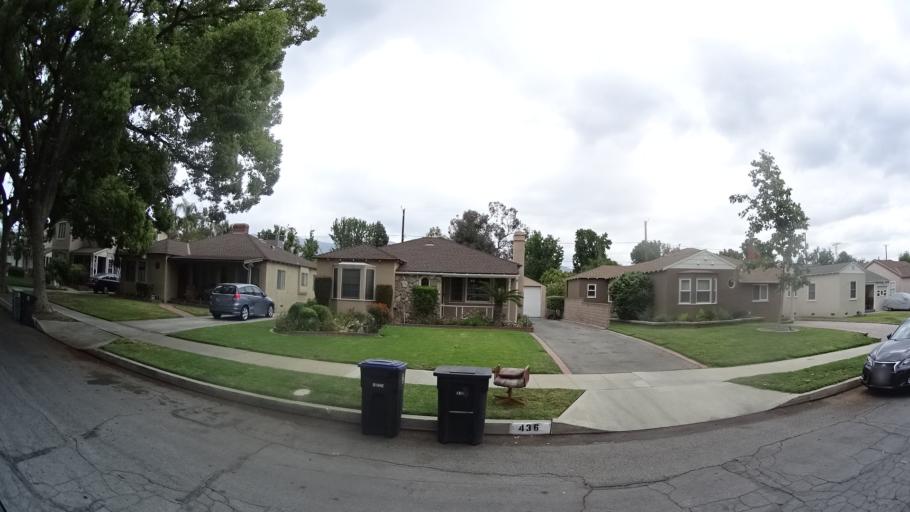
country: US
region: California
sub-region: Los Angeles County
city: Burbank
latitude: 34.1726
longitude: -118.3255
